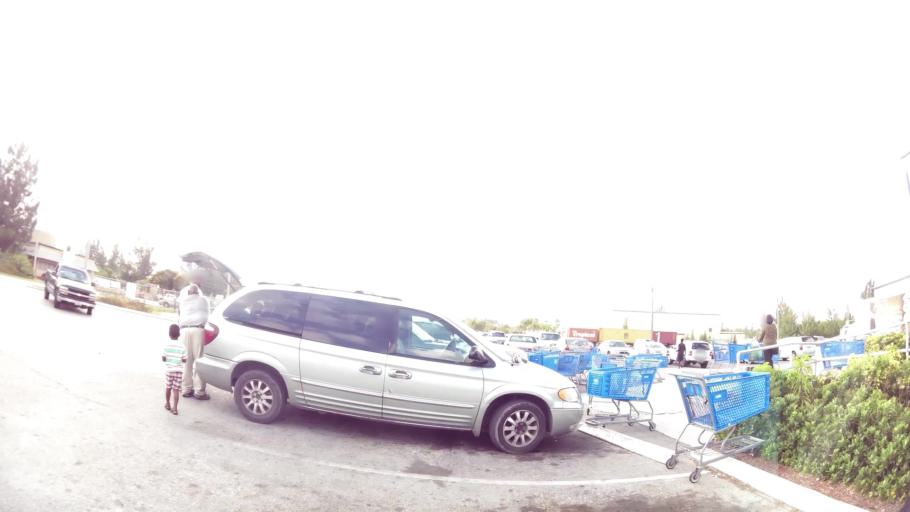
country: BS
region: Freeport
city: Freeport
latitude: 26.5388
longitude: -78.7106
